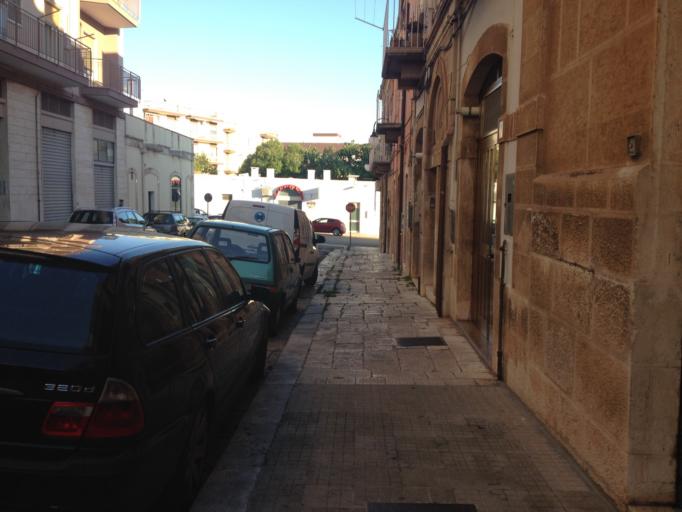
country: IT
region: Apulia
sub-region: Provincia di Bari
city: Putignano
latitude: 40.8482
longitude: 17.1216
